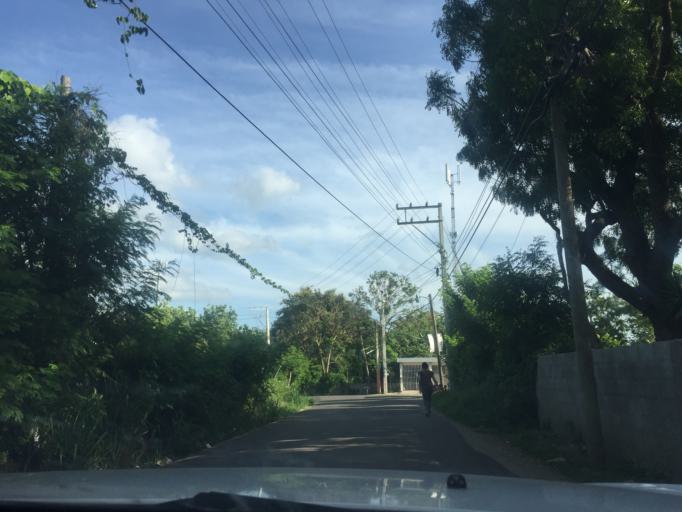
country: DO
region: Santiago
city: Tamboril
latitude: 19.4815
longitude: -70.6378
